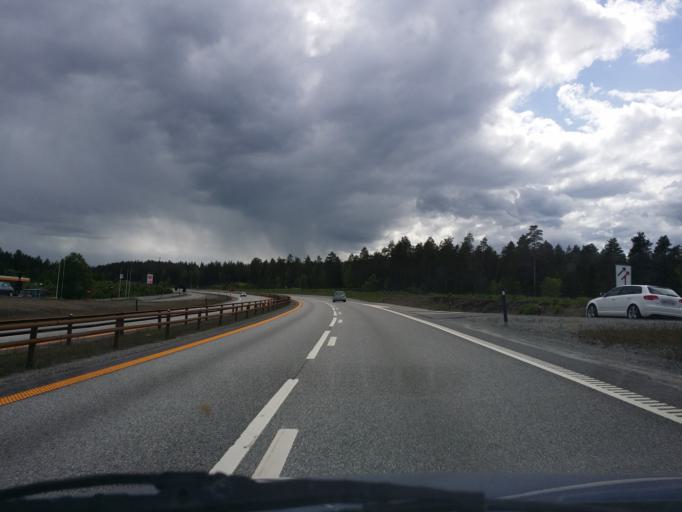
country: NO
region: Akershus
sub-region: Eidsvoll
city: Raholt
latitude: 60.3133
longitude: 11.1445
